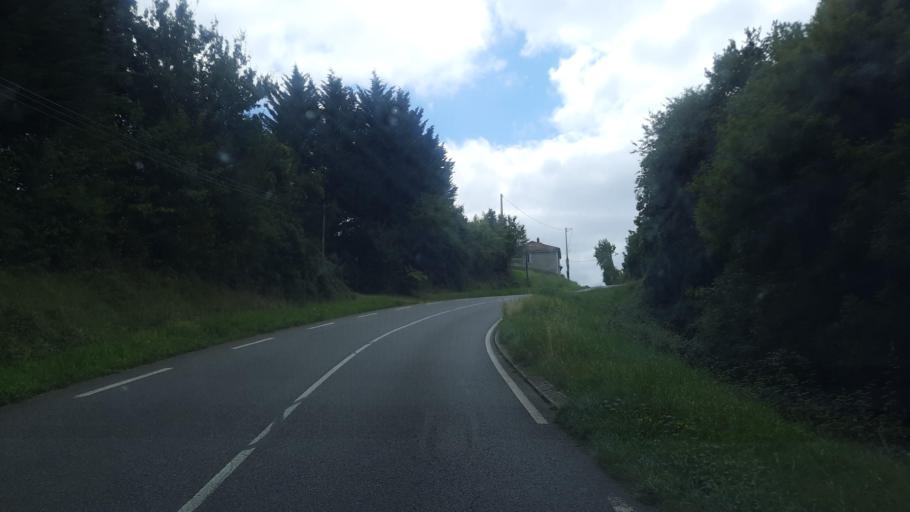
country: FR
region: Midi-Pyrenees
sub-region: Departement des Hautes-Pyrenees
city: Trie-sur-Baise
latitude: 43.3086
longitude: 0.3796
